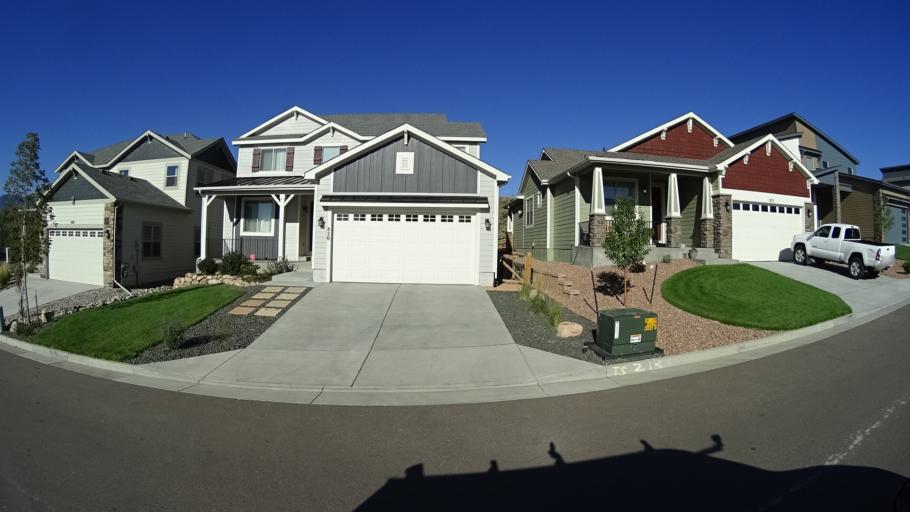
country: US
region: Colorado
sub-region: El Paso County
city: Colorado Springs
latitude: 38.8451
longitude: -104.8377
